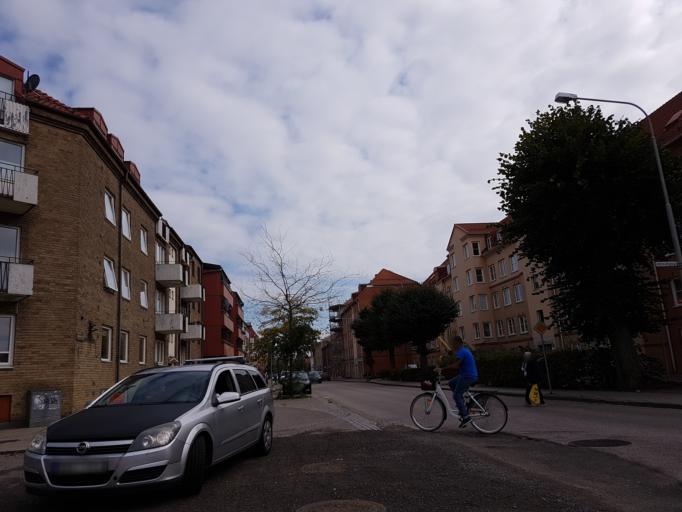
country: SE
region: Skane
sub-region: Landskrona
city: Landskrona
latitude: 55.8760
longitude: 12.8370
